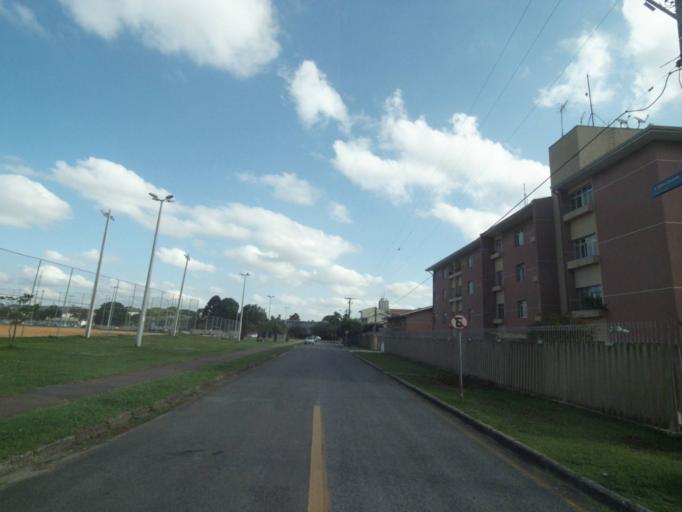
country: BR
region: Parana
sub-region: Curitiba
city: Curitiba
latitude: -25.4964
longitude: -49.3224
